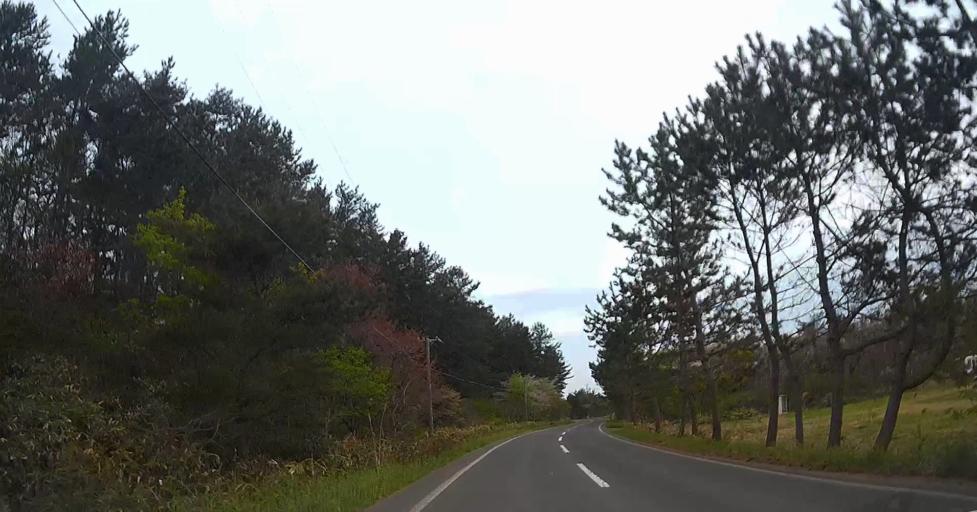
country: JP
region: Aomori
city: Shimokizukuri
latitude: 40.9370
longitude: 140.3261
